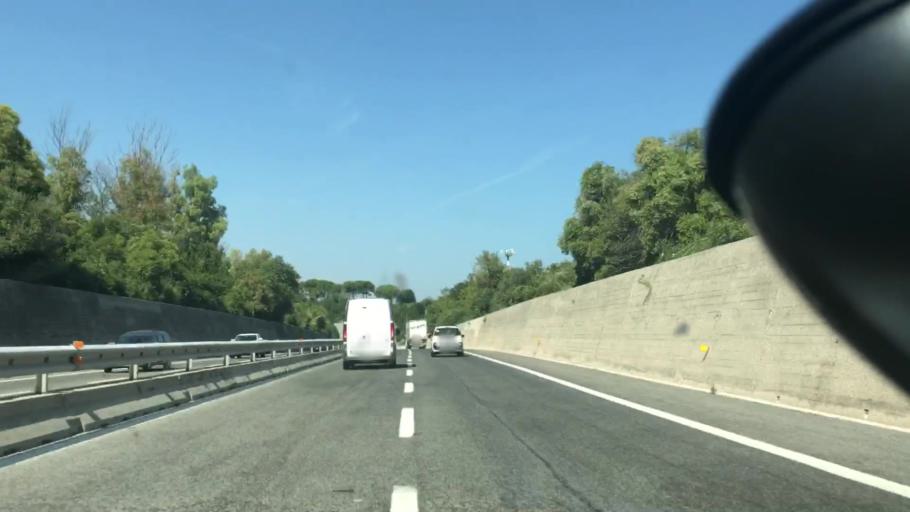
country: IT
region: Abruzzo
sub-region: Provincia di Chieti
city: Tollo
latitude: 42.3674
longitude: 14.3204
